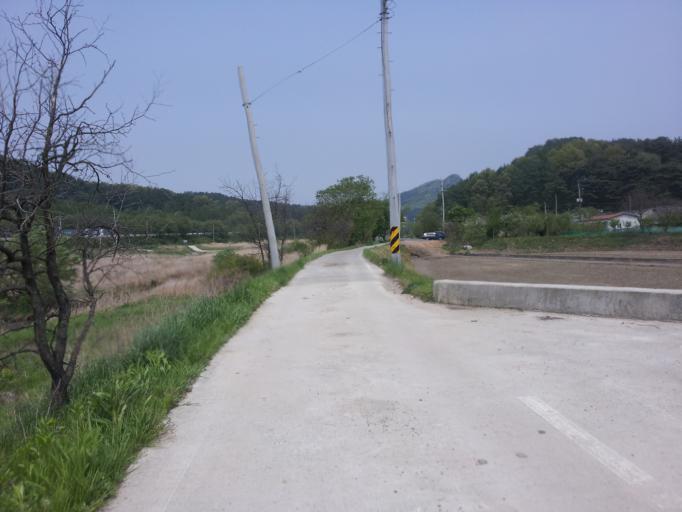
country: KR
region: Daejeon
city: Daejeon
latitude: 36.2583
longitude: 127.2829
